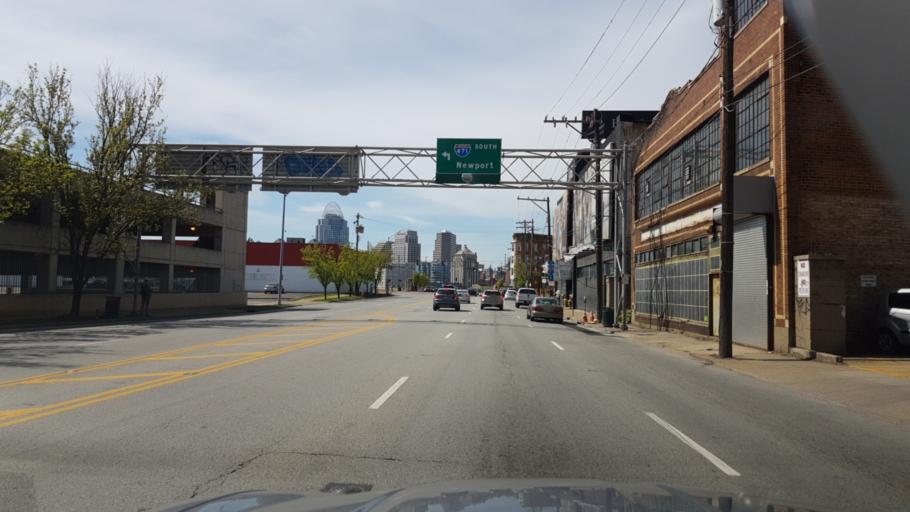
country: US
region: Kentucky
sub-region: Campbell County
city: Newport
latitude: 39.1126
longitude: -84.5029
